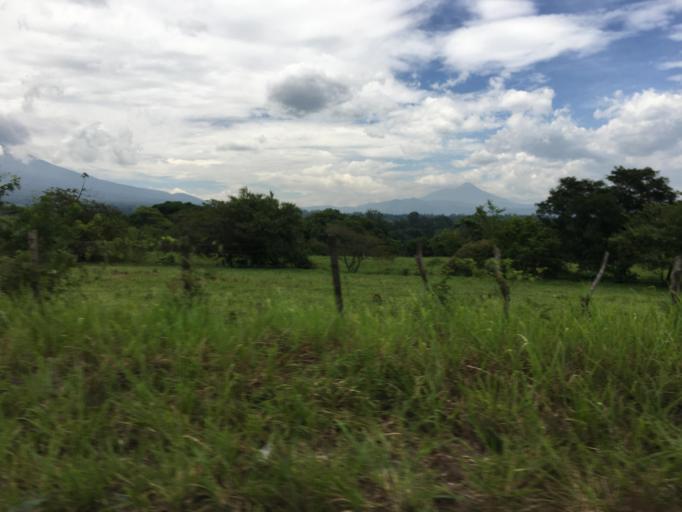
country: GT
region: Escuintla
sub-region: Municipio de Escuintla
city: Escuintla
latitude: 14.3676
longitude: -90.8133
